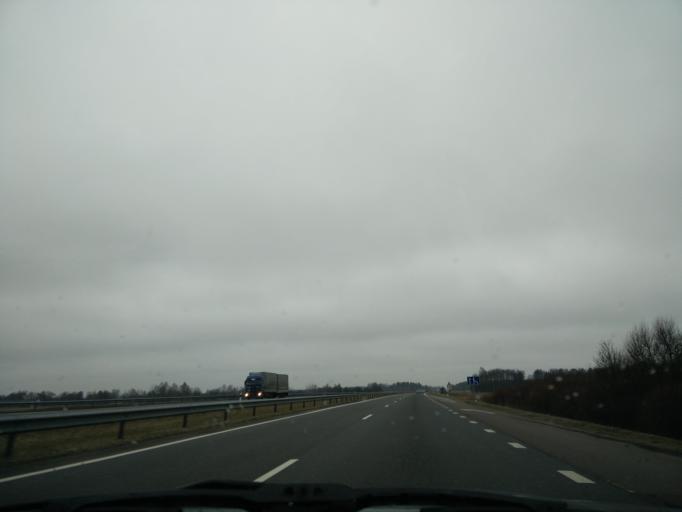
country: LT
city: Raseiniai
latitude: 55.3868
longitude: 22.8980
